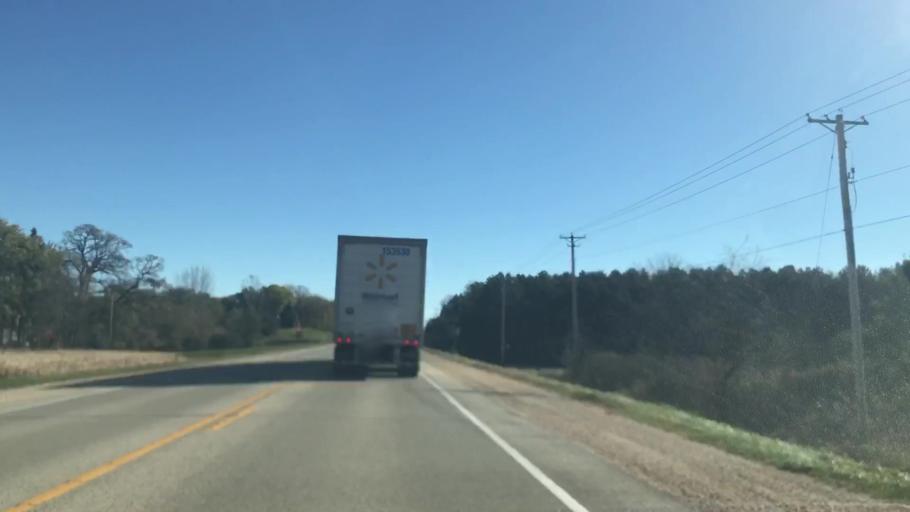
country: US
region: Wisconsin
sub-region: Dodge County
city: Juneau
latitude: 43.4450
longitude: -88.7087
